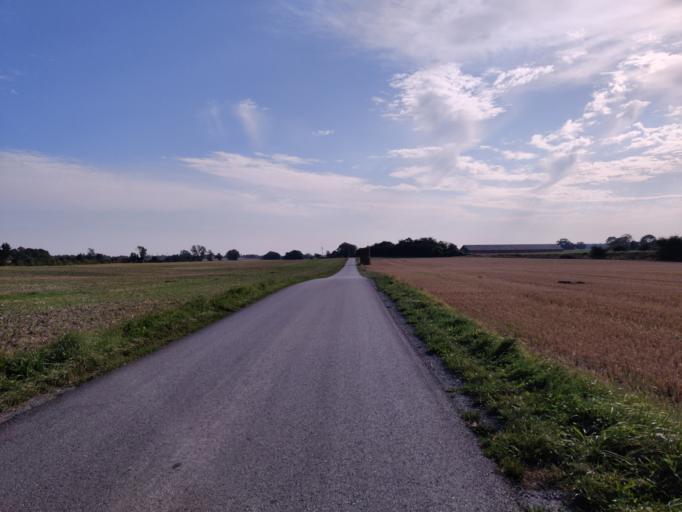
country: DK
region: Zealand
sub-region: Guldborgsund Kommune
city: Nykobing Falster
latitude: 54.6964
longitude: 11.9051
